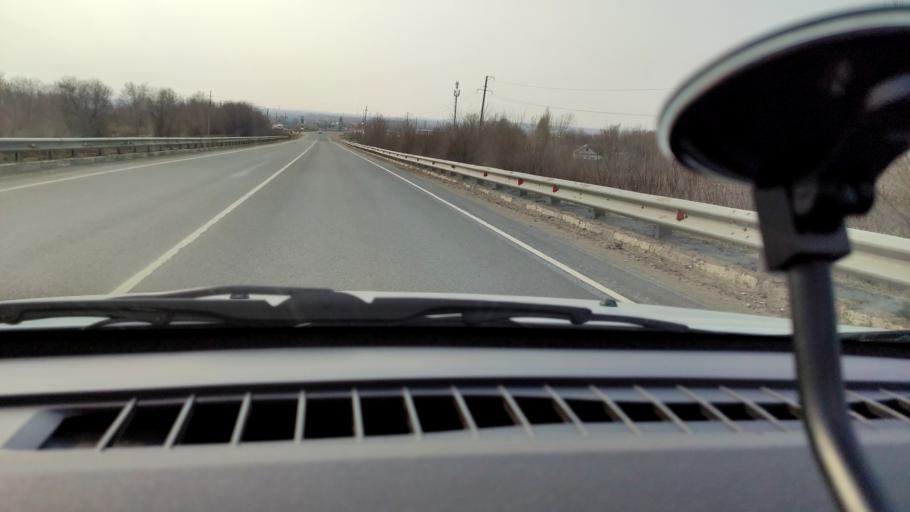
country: RU
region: Samara
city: Dubovyy Umet
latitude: 53.0856
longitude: 50.3198
